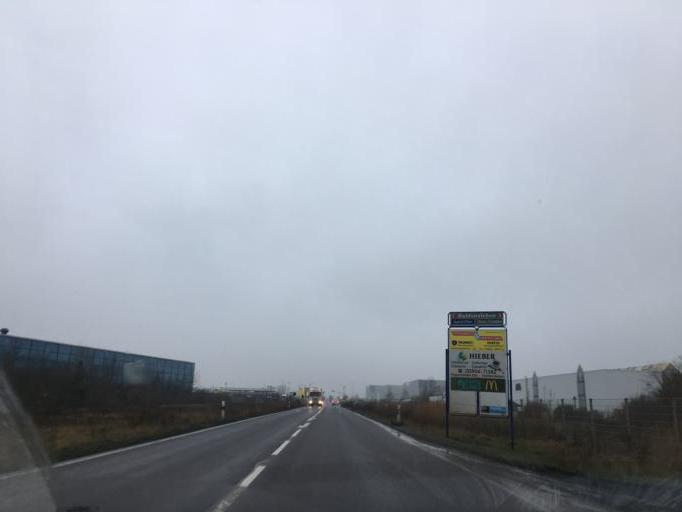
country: DE
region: Saxony-Anhalt
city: Haldensleben I
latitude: 52.2764
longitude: 11.4474
